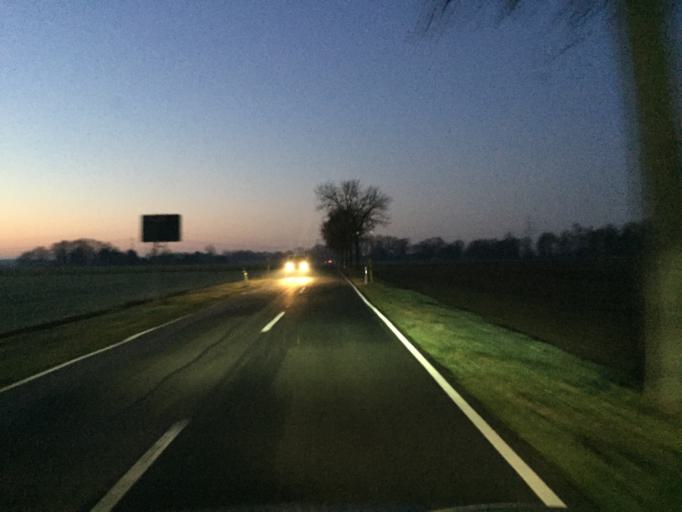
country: DE
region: Lower Saxony
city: Steyerberg
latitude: 52.5593
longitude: 9.0289
